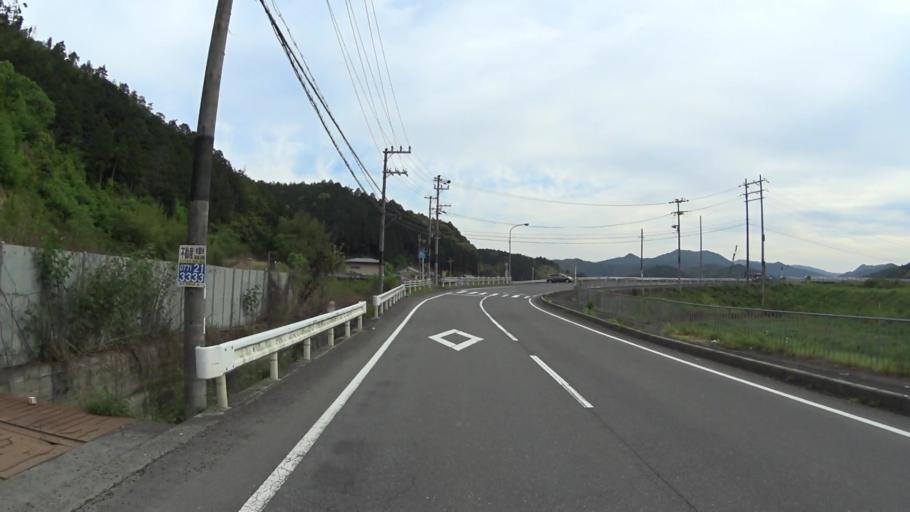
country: JP
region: Kyoto
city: Kameoka
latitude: 35.1039
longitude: 135.5170
